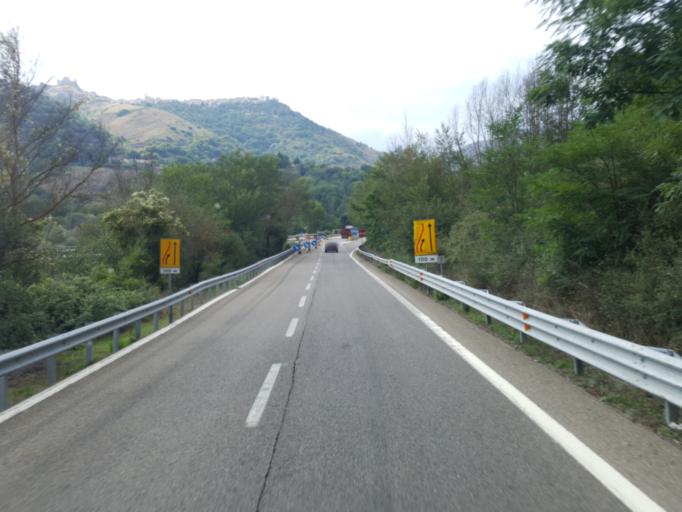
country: IT
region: Basilicate
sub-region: Provincia di Potenza
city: Brindisi Montagna
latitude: 40.6108
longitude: 15.9584
